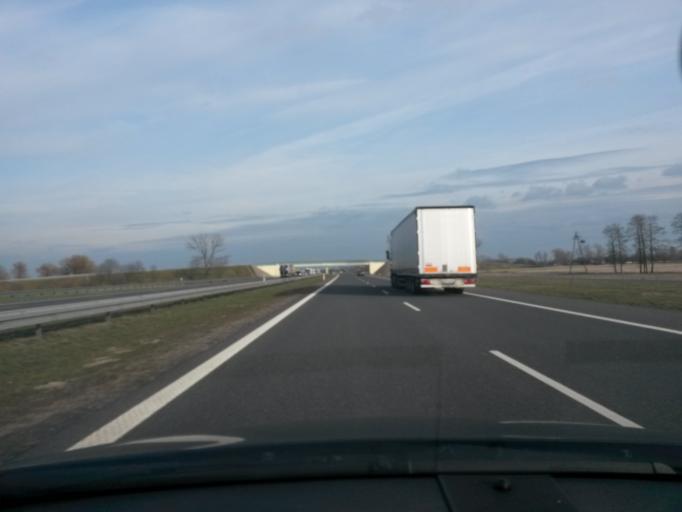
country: PL
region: Lodz Voivodeship
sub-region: Powiat poddebicki
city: Wartkowice
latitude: 52.0060
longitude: 18.9828
